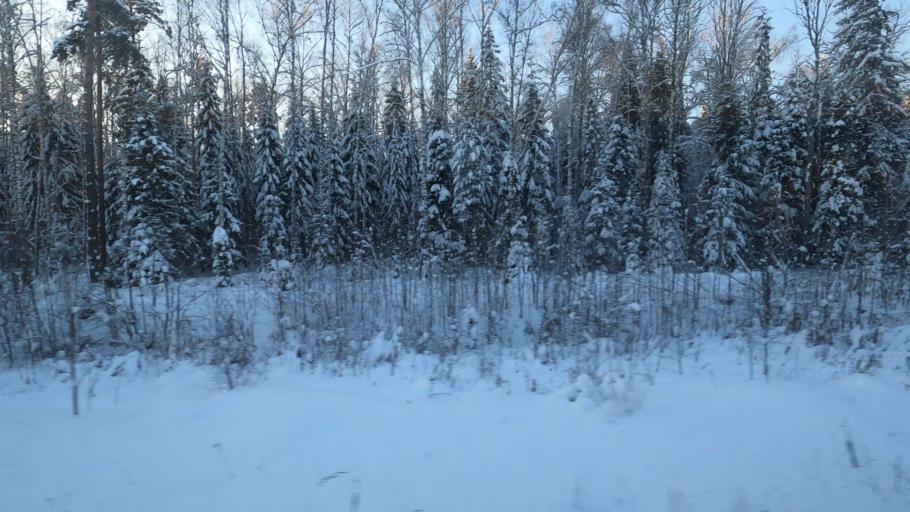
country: RU
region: Moskovskaya
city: Zhukovka
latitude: 56.5036
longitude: 37.5534
